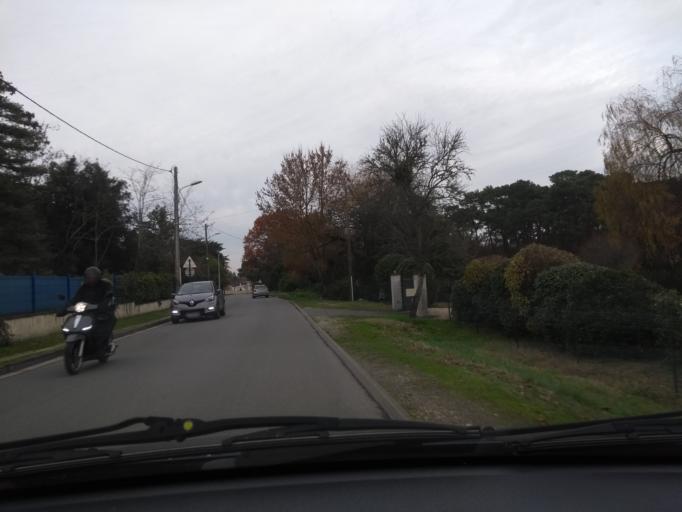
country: FR
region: Aquitaine
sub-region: Departement de la Gironde
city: Gradignan
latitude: 44.7598
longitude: -0.6122
